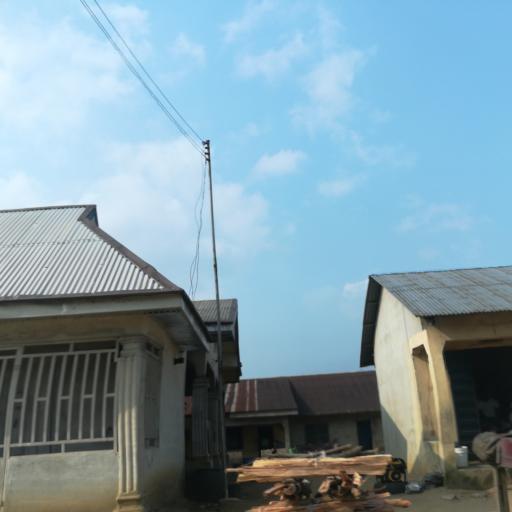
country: NG
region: Rivers
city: Okrika
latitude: 4.7780
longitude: 7.1565
